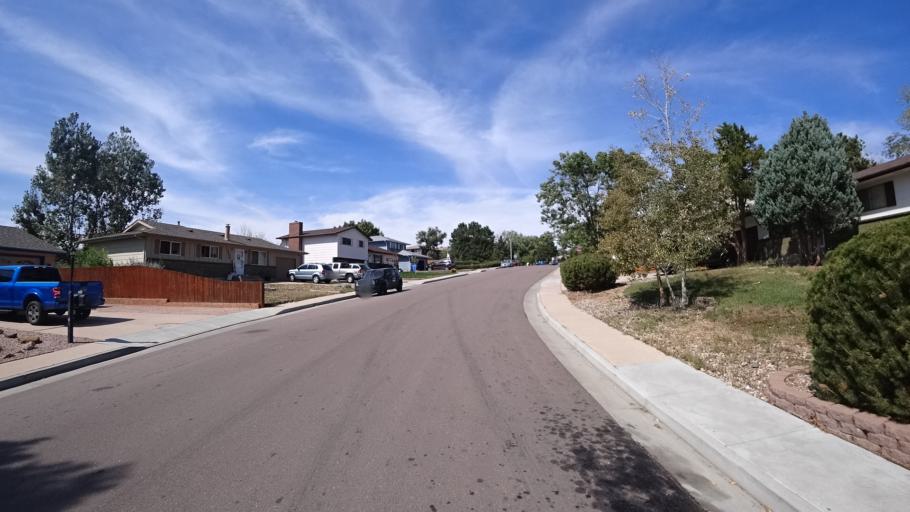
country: US
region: Colorado
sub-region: El Paso County
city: Colorado Springs
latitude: 38.9080
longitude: -104.7727
